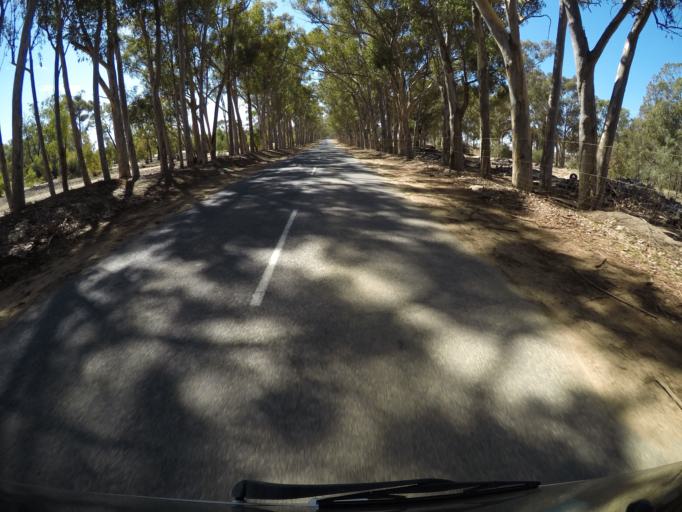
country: ZA
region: Western Cape
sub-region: City of Cape Town
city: Sunset Beach
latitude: -33.7660
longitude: 18.5502
